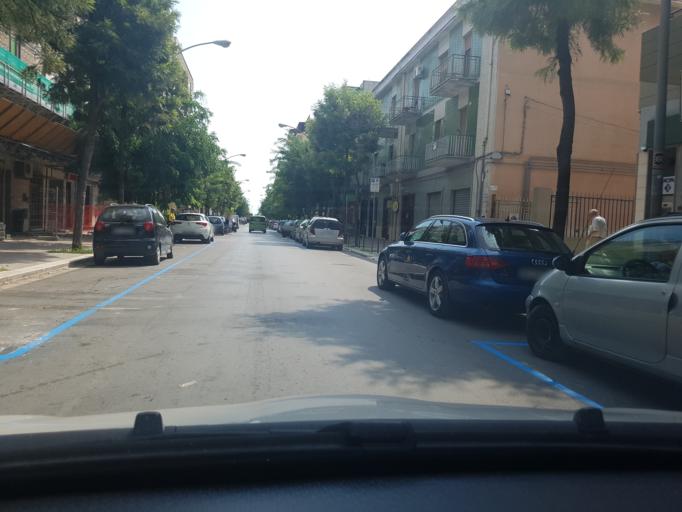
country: IT
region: Apulia
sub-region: Provincia di Foggia
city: Cerignola
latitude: 41.2635
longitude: 15.9094
